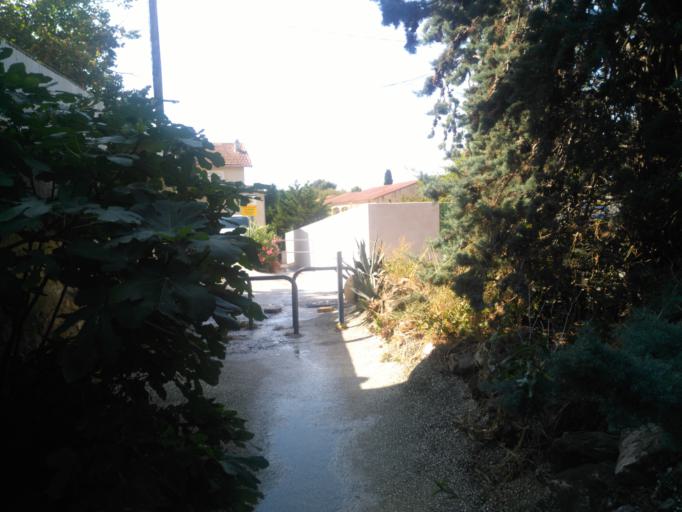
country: FR
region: Provence-Alpes-Cote d'Azur
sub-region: Departement du Var
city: Bandol
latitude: 43.1391
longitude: 5.7460
